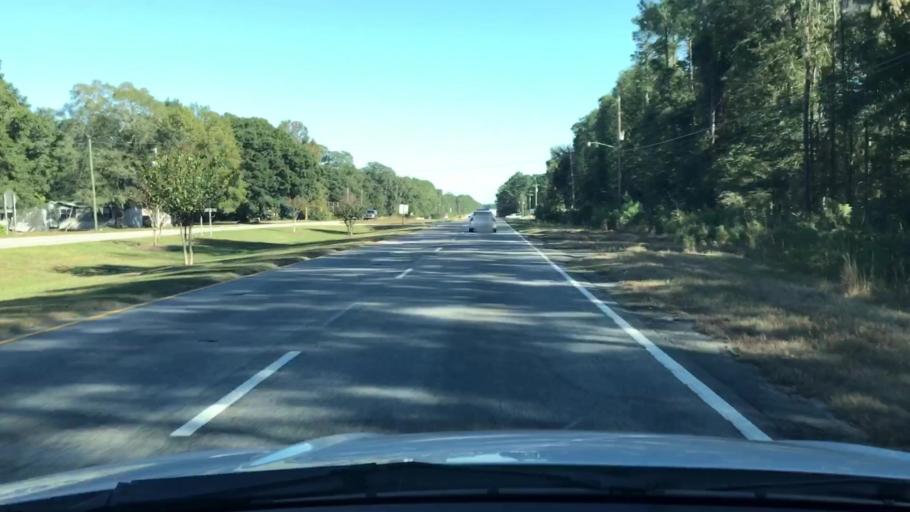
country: US
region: South Carolina
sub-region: Charleston County
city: Ravenel
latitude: 32.7834
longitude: -80.2070
